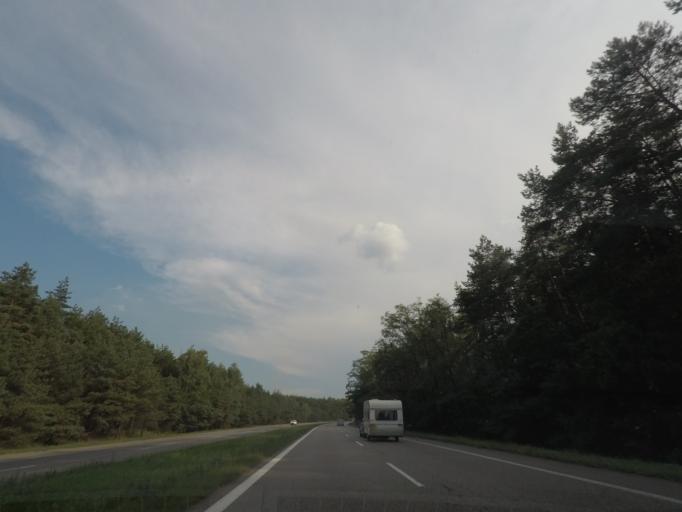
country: PL
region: Silesian Voivodeship
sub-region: Dabrowa Gornicza
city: Dabrowa Gornicza
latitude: 50.3706
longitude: 19.2484
